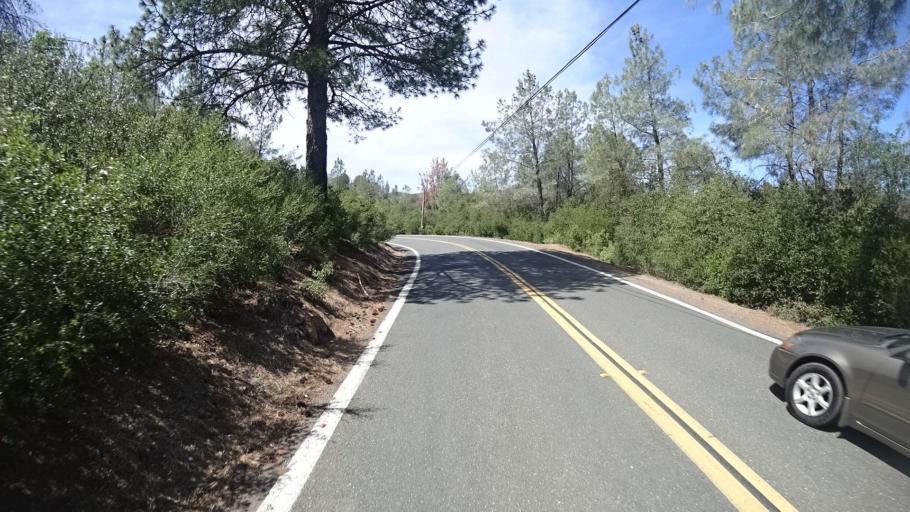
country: US
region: California
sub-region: Lake County
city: Clearlake
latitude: 38.9218
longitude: -122.6647
